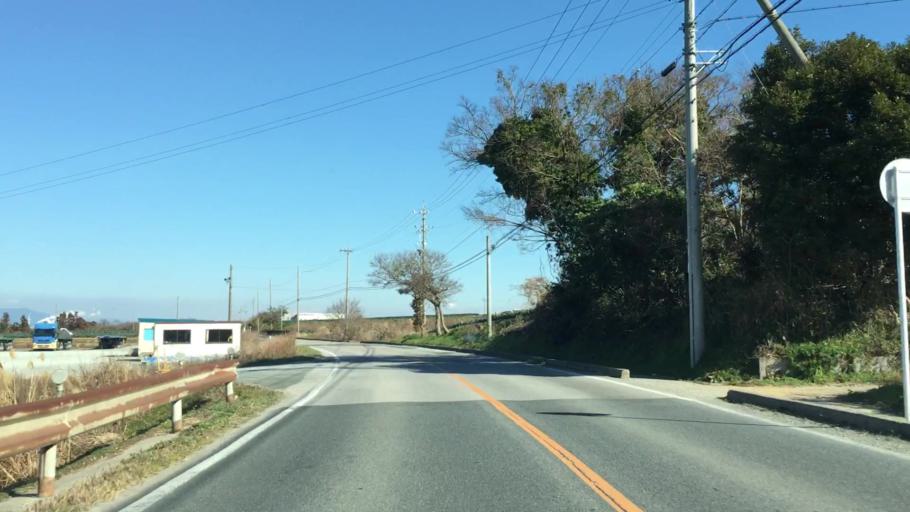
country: JP
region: Aichi
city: Tahara
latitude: 34.6887
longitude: 137.2532
